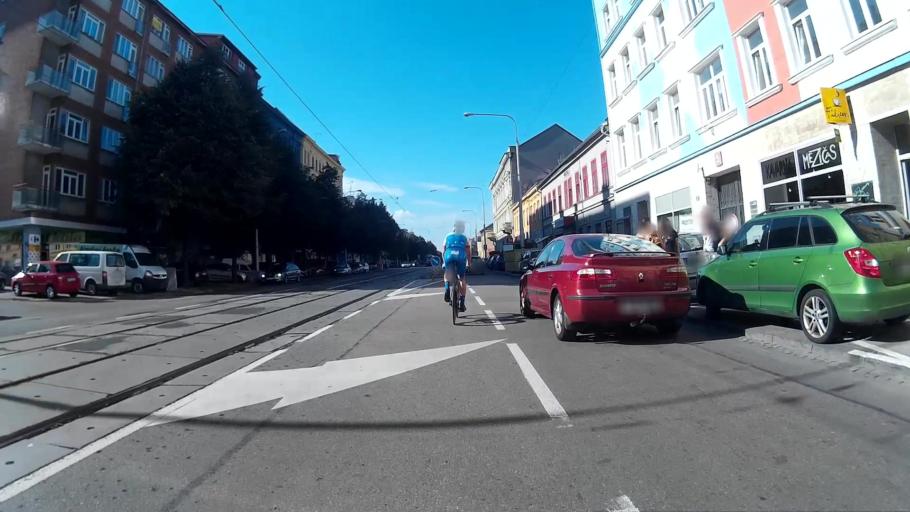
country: CZ
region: South Moravian
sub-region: Mesto Brno
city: Brno
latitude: 49.2095
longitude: 16.6035
